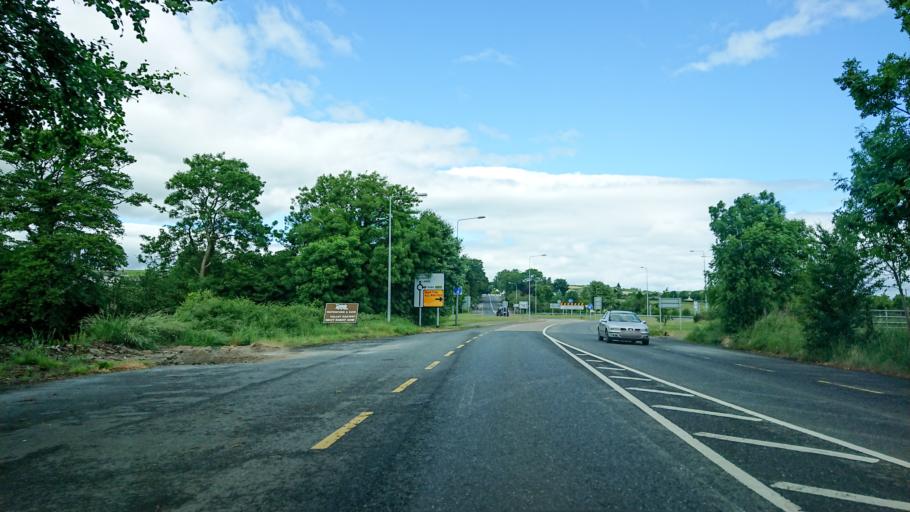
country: IE
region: Leinster
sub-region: Kilkenny
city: Mooncoin
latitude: 52.2358
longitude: -7.2462
